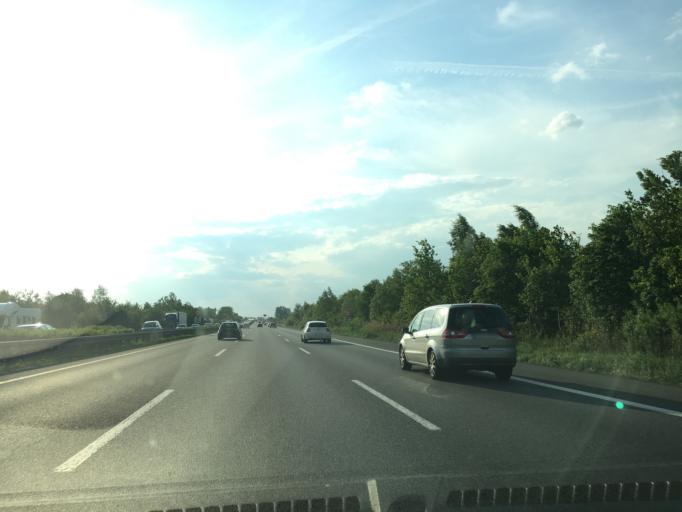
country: DE
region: Lower Saxony
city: Arpke
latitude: 52.3747
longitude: 10.0484
